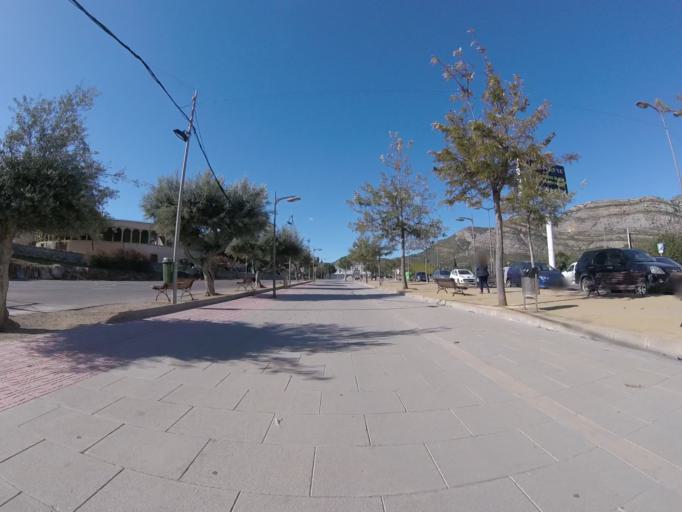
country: ES
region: Valencia
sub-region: Provincia de Castello
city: Orpesa/Oropesa del Mar
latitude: 40.0935
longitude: 0.1321
